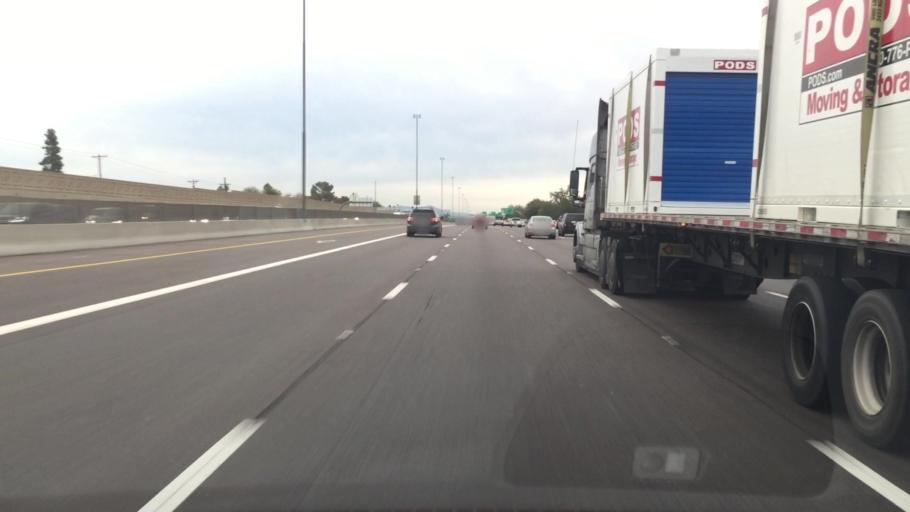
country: US
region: Arizona
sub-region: Maricopa County
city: Tempe
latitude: 33.3842
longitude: -111.9232
